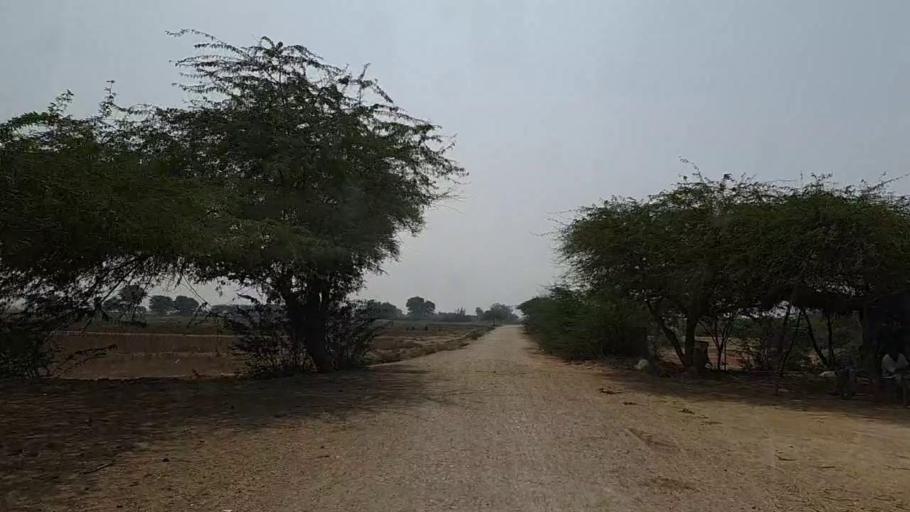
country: PK
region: Sindh
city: Naukot
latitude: 24.8245
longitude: 69.3612
